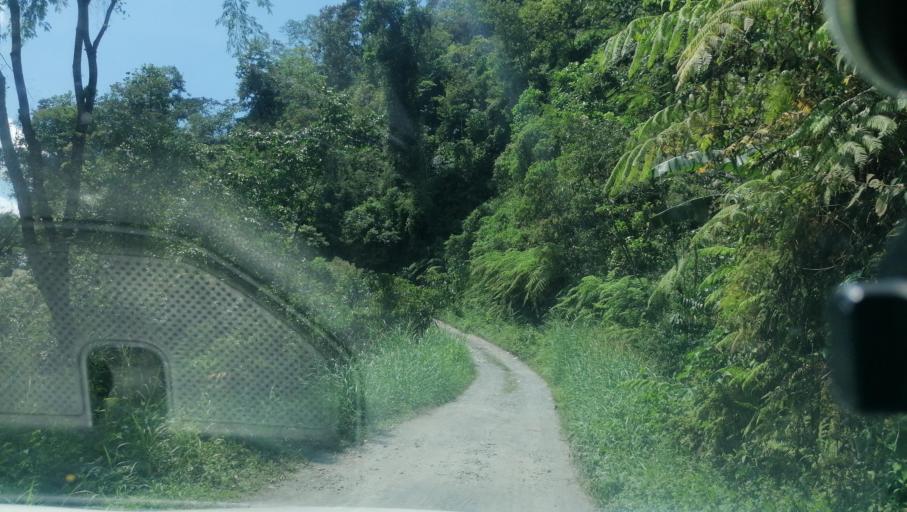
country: MX
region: Chiapas
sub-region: Union Juarez
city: Santo Domingo
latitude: 15.0684
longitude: -92.1377
